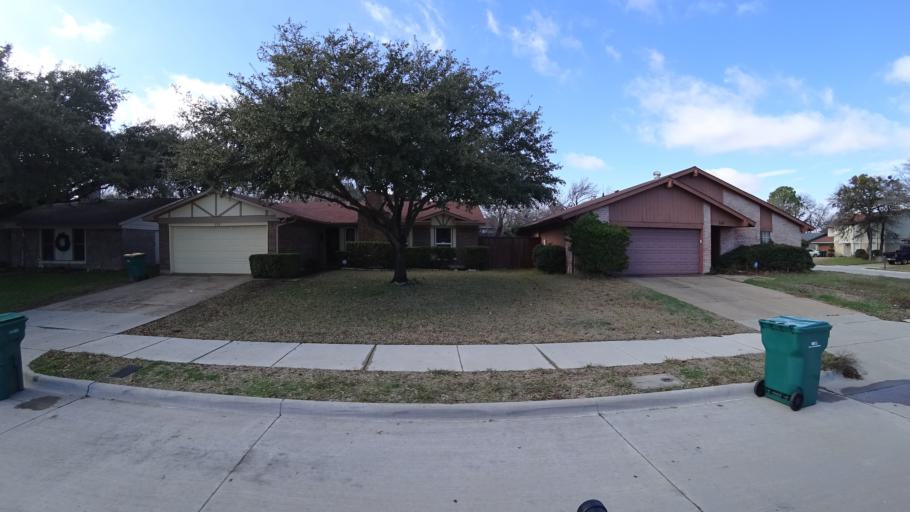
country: US
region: Texas
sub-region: Denton County
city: Lewisville
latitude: 33.0329
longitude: -97.0049
